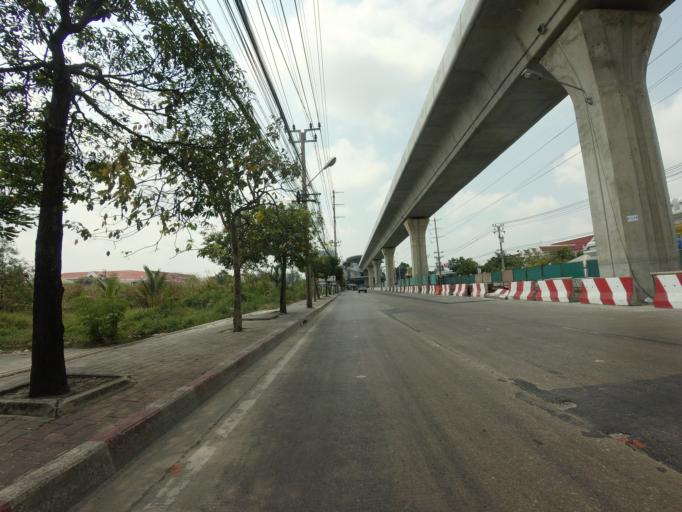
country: TH
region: Samut Prakan
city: Samut Prakan
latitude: 13.6107
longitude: 100.5942
